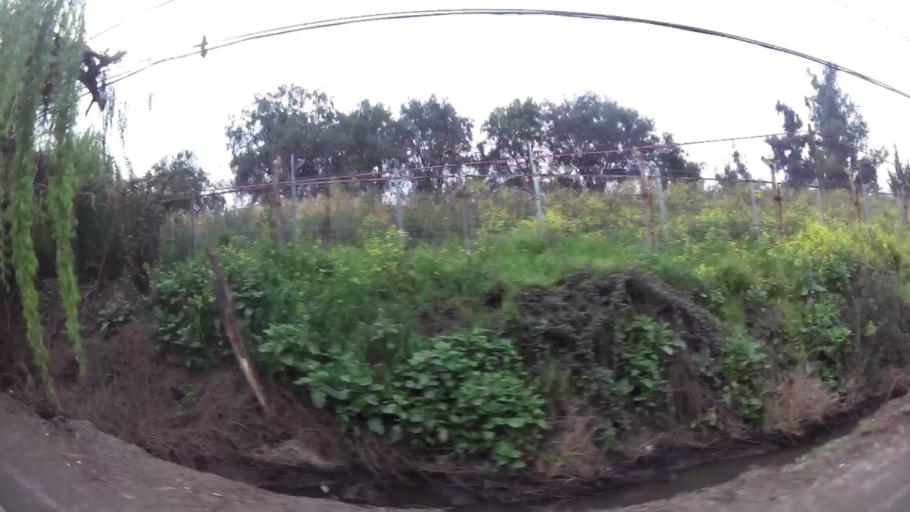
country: CL
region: Santiago Metropolitan
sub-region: Provincia de Chacabuco
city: Chicureo Abajo
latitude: -33.2575
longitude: -70.7625
